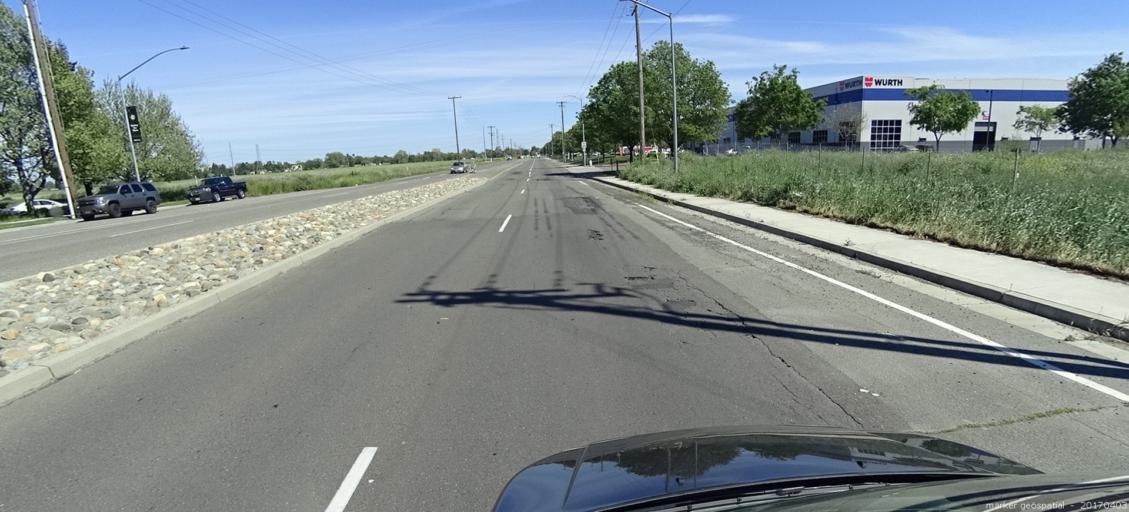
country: US
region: California
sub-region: Sacramento County
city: Rio Linda
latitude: 38.6562
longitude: -121.4938
